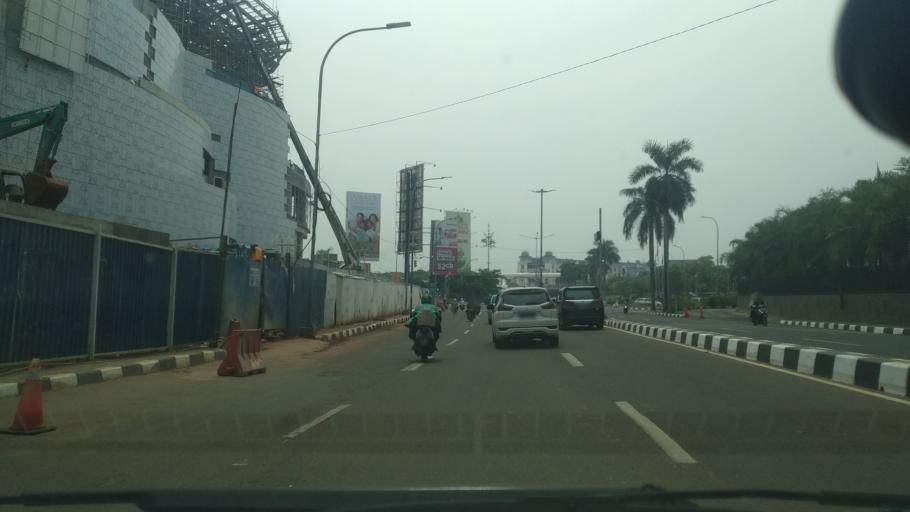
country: ID
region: Banten
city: South Tangerang
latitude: -6.2642
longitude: 106.7826
